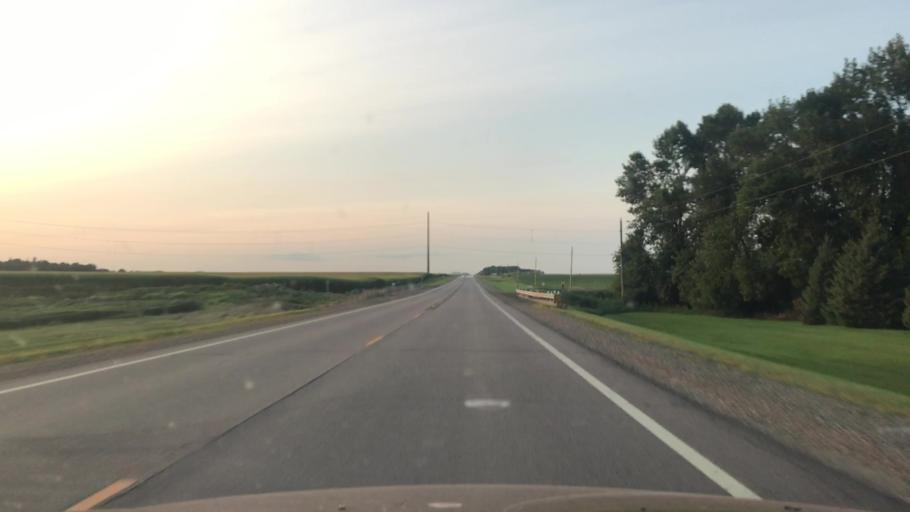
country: US
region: Minnesota
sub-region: Redwood County
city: Redwood Falls
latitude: 44.4294
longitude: -95.1176
